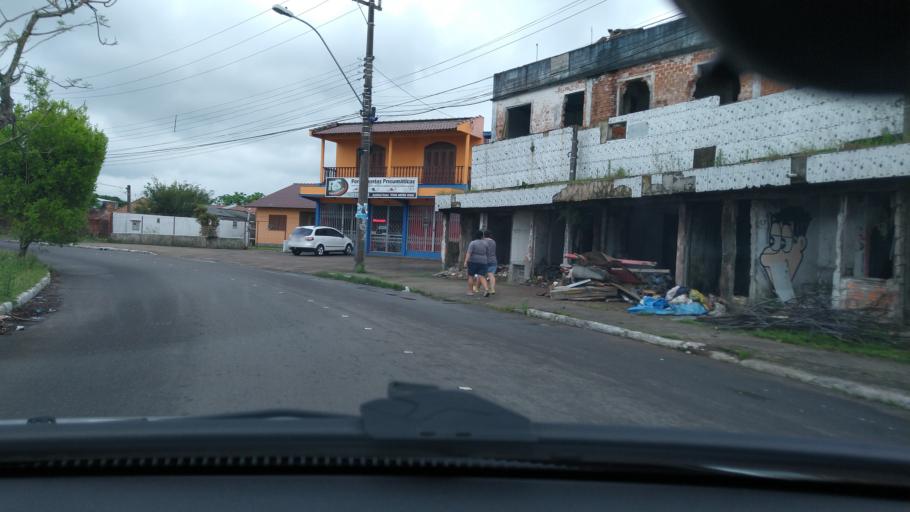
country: BR
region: Rio Grande do Sul
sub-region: Canoas
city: Canoas
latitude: -29.9009
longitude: -51.2167
